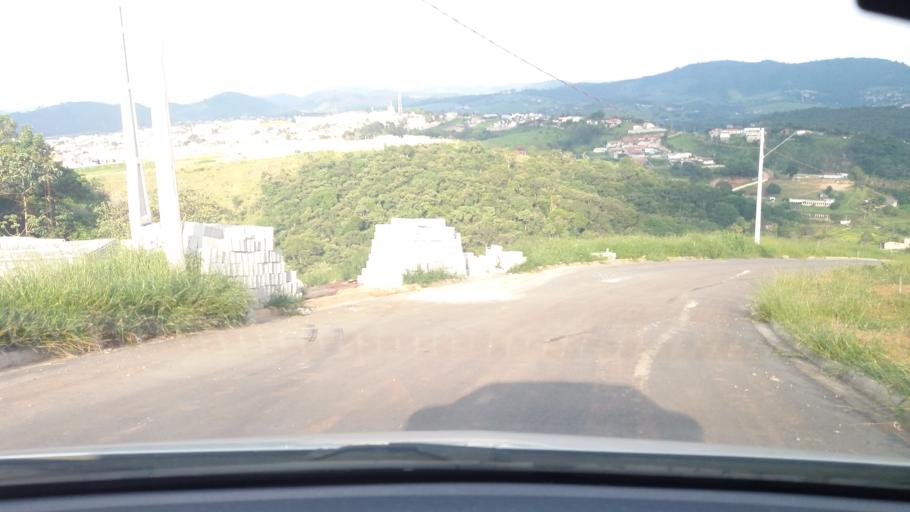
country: BR
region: Sao Paulo
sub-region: Bom Jesus Dos Perdoes
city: Bom Jesus dos Perdoes
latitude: -23.1518
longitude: -46.4779
